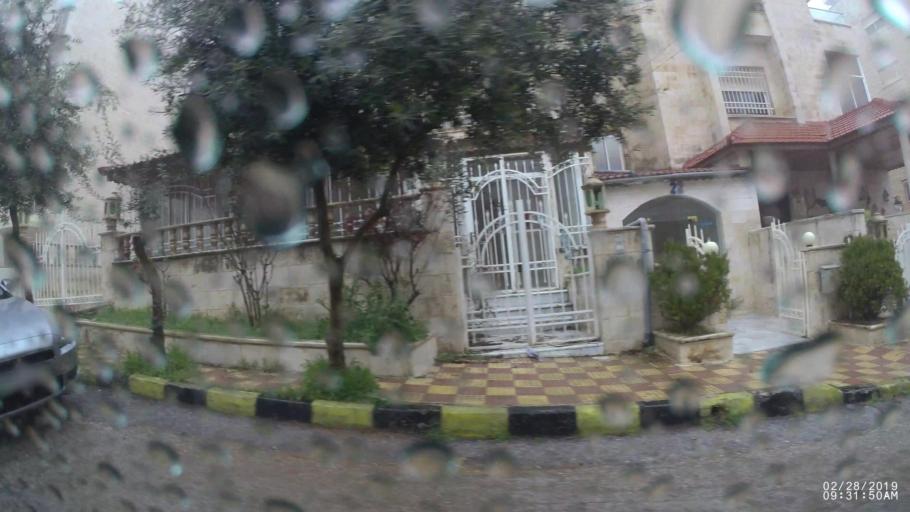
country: JO
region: Amman
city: Al Jubayhah
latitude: 32.0066
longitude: 35.8836
